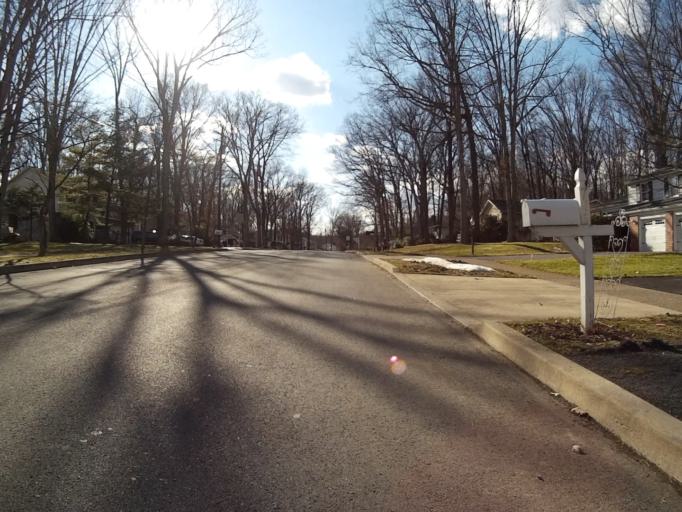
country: US
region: Pennsylvania
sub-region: Centre County
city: Park Forest Village
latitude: 40.8009
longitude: -77.9020
